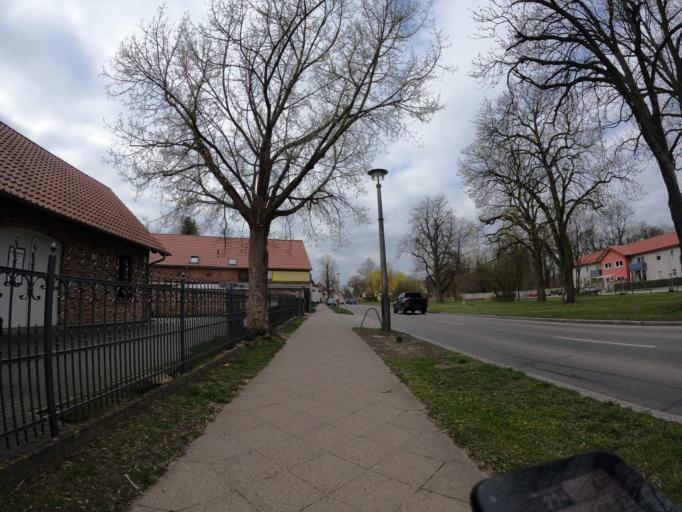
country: DE
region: Brandenburg
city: Neuenhagen
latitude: 52.5341
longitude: 13.6955
